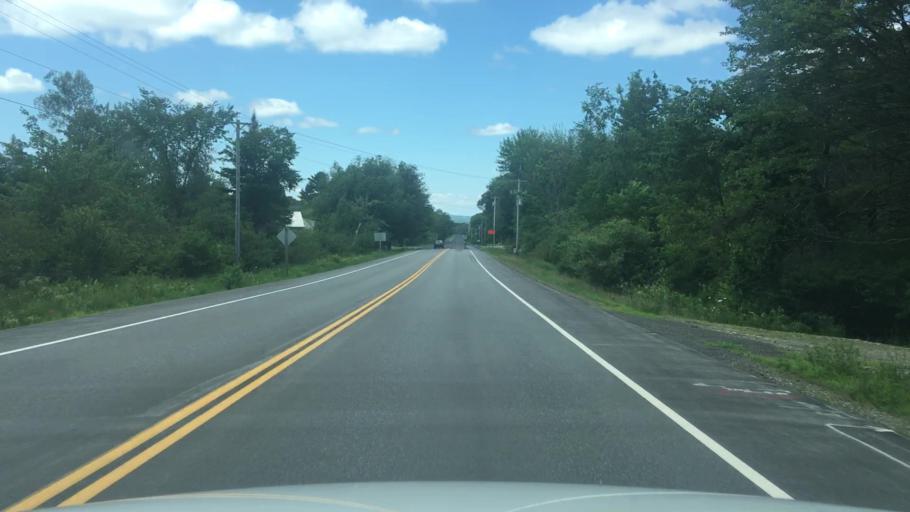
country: US
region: Maine
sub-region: Waldo County
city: Searsmont
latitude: 44.3979
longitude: -69.1424
